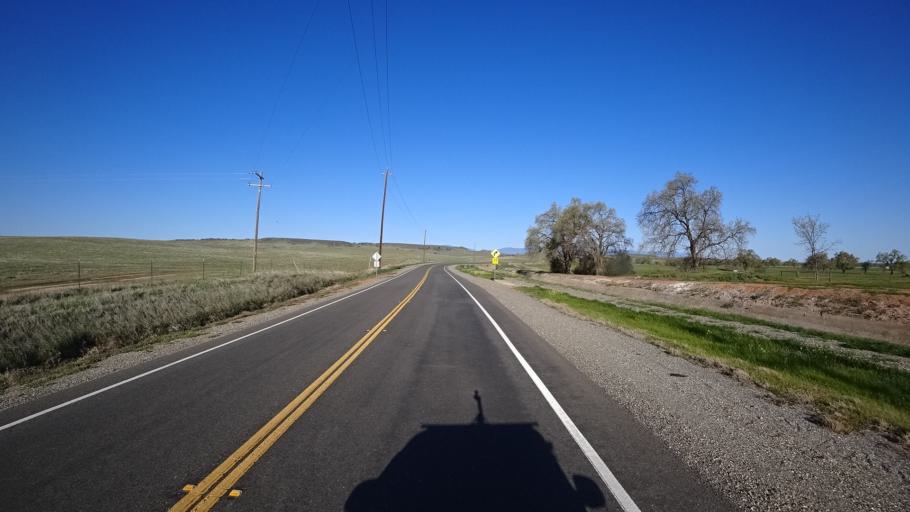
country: US
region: California
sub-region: Glenn County
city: Orland
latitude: 39.7878
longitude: -122.3043
